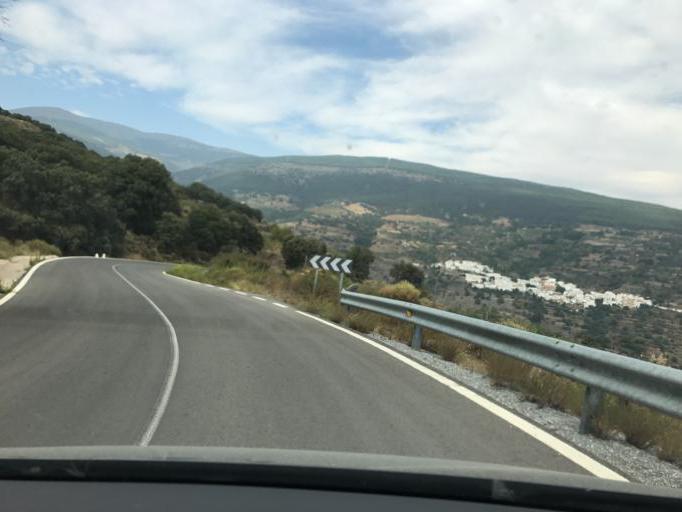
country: ES
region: Andalusia
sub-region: Provincia de Almeria
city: Bayarcal
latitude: 37.0221
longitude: -3.0084
